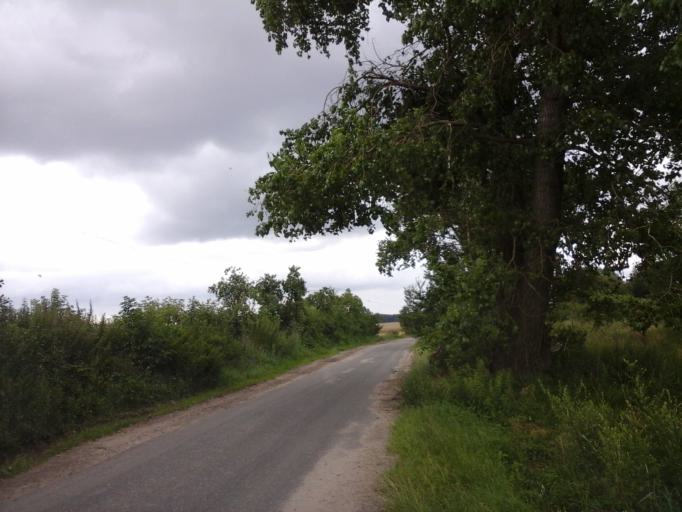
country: PL
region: West Pomeranian Voivodeship
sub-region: Powiat choszczenski
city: Krzecin
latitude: 52.9984
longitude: 15.4268
